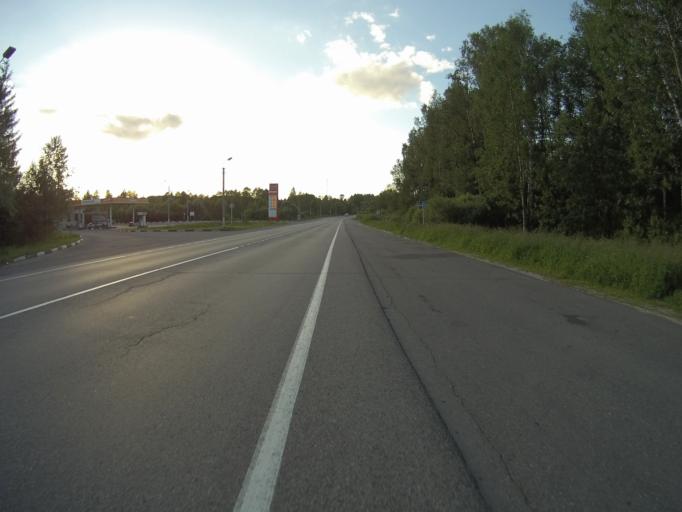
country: RU
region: Vladimir
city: Golovino
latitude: 55.9214
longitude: 40.6032
